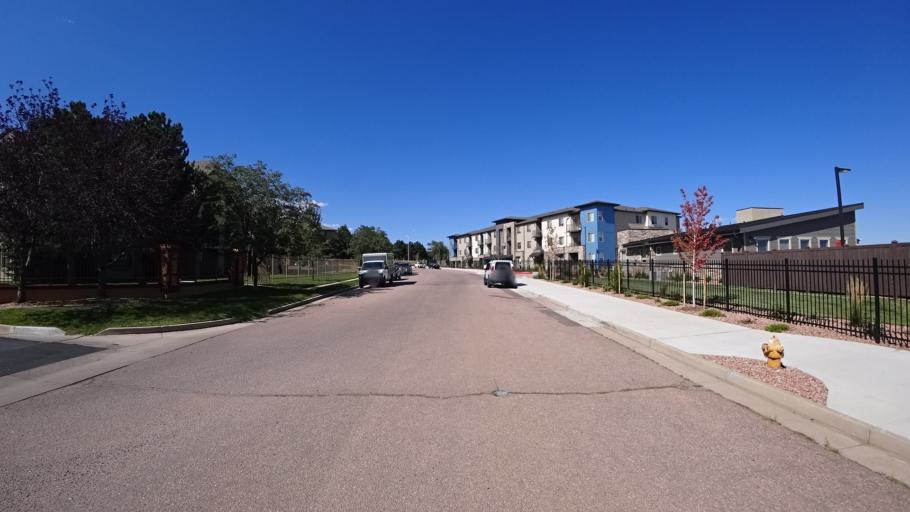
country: US
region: Colorado
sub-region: El Paso County
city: Colorado Springs
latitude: 38.8736
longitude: -104.8518
